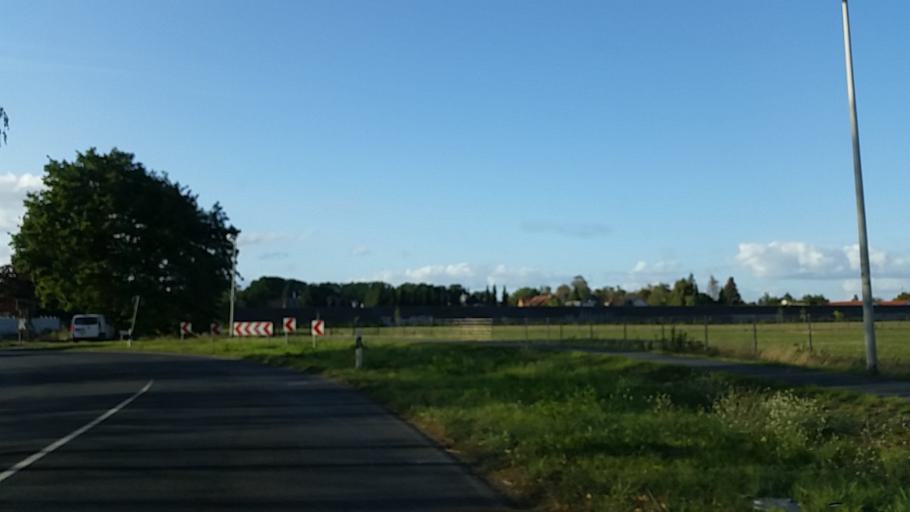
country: DE
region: Lower Saxony
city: Braunschweig
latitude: 52.3154
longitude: 10.5336
